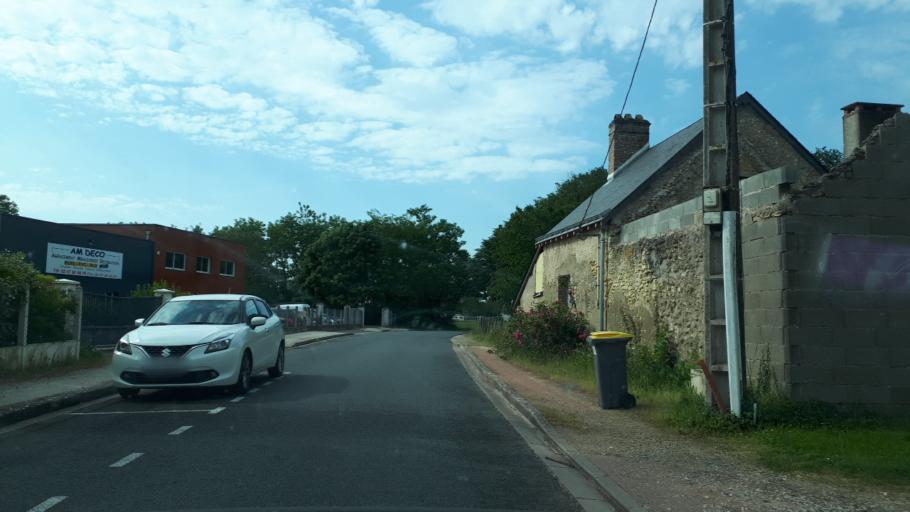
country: FR
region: Centre
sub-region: Departement d'Indre-et-Loire
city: Monnaie
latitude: 47.4932
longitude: 0.7753
